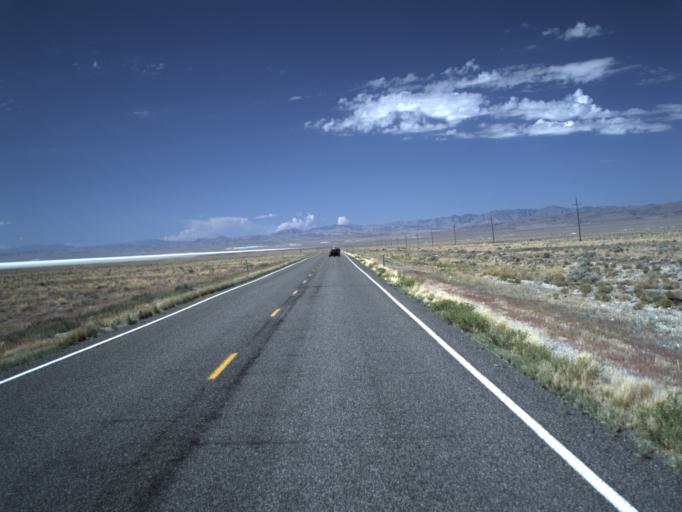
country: US
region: Utah
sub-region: Millard County
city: Delta
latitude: 39.1377
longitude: -113.0907
